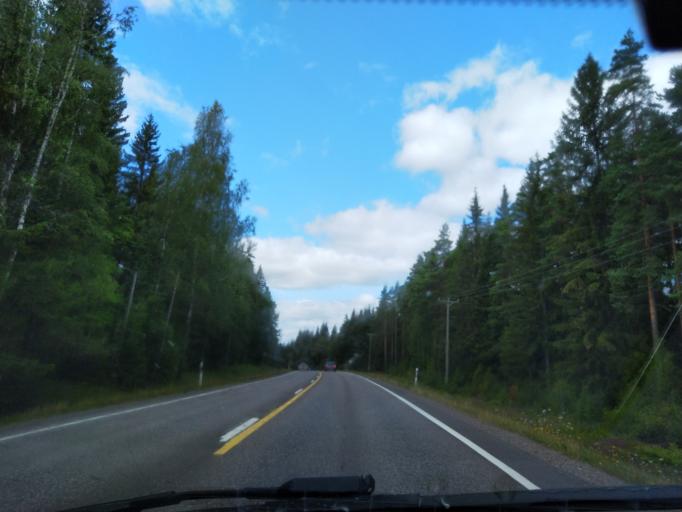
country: FI
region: Haeme
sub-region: Haemeenlinna
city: Renko
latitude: 60.7593
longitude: 24.2928
